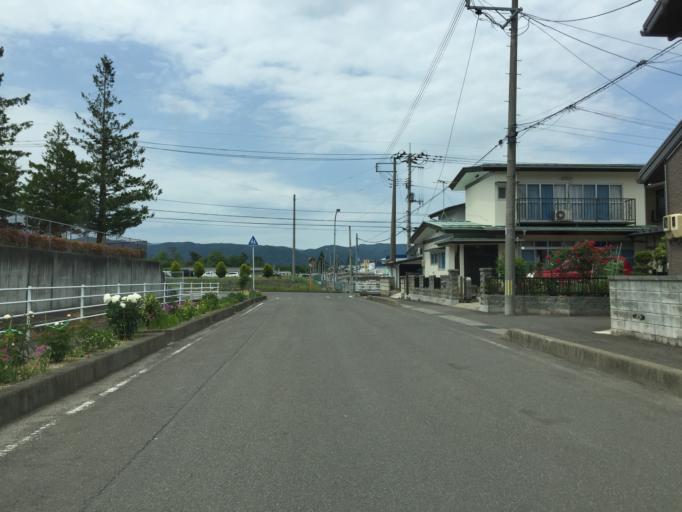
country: JP
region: Fukushima
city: Fukushima-shi
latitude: 37.7385
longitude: 140.4019
